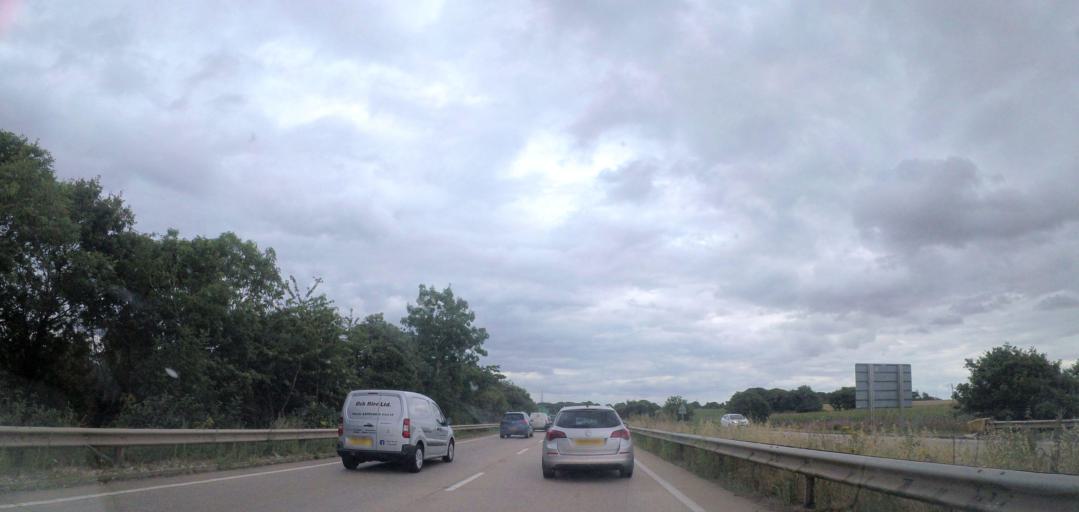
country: GB
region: England
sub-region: Norfolk
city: Hethersett
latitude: 52.5933
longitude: 1.2050
